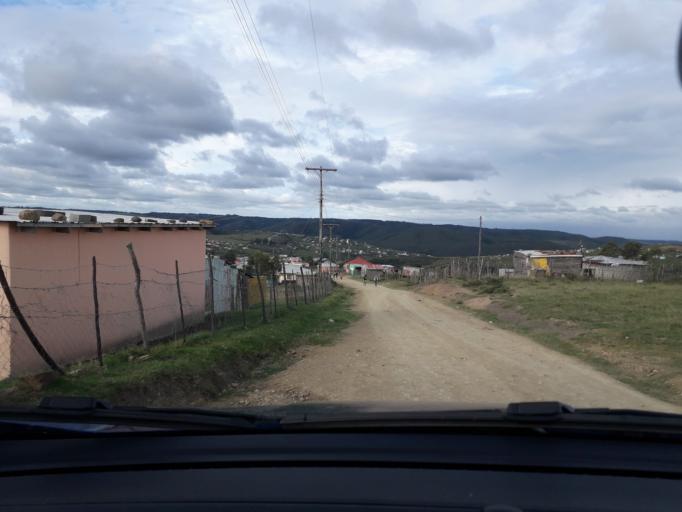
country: ZA
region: Eastern Cape
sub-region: Buffalo City Metropolitan Municipality
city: East London
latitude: -32.8059
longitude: 27.9580
